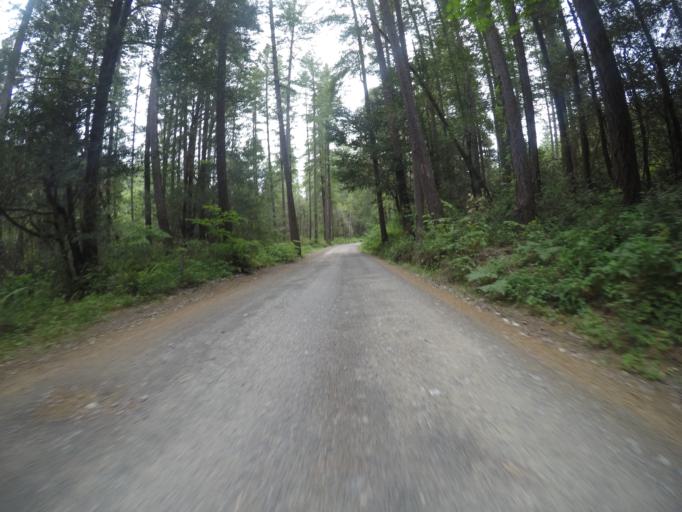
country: US
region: California
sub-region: Del Norte County
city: Bertsch-Oceanview
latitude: 41.6909
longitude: -123.9052
